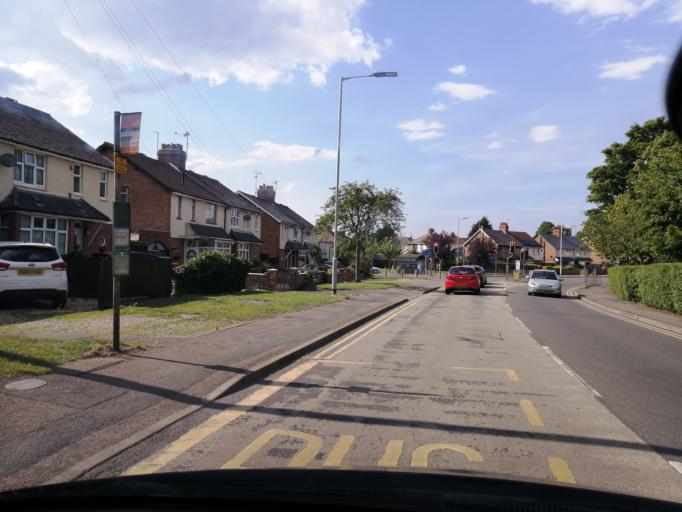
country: GB
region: England
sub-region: Peterborough
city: Peterborough
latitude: 52.5571
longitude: -0.2496
